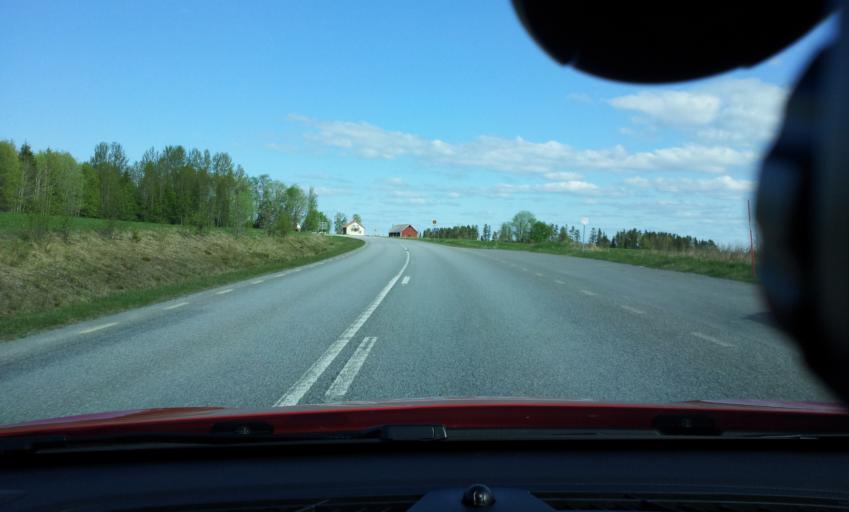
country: SE
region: Jaemtland
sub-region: Krokoms Kommun
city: Krokom
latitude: 63.1256
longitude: 14.2927
